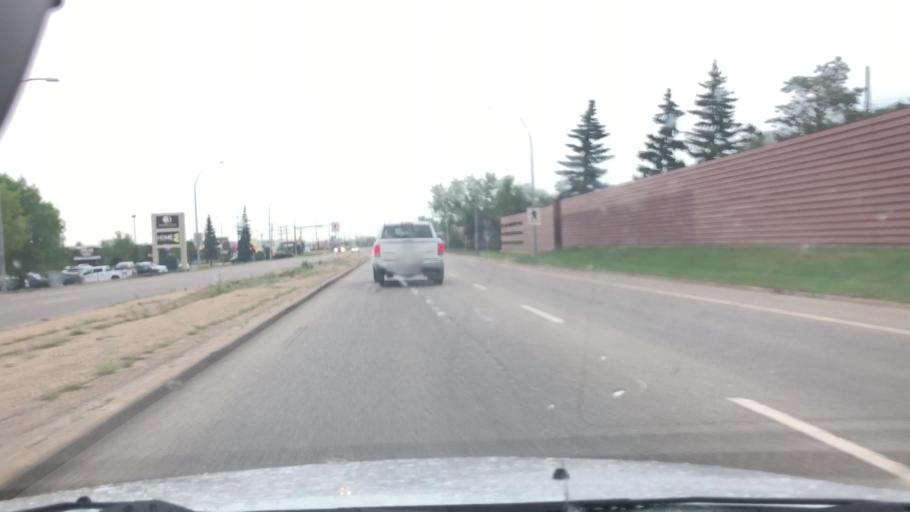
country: CA
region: Alberta
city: St. Albert
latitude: 53.5543
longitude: -113.6064
